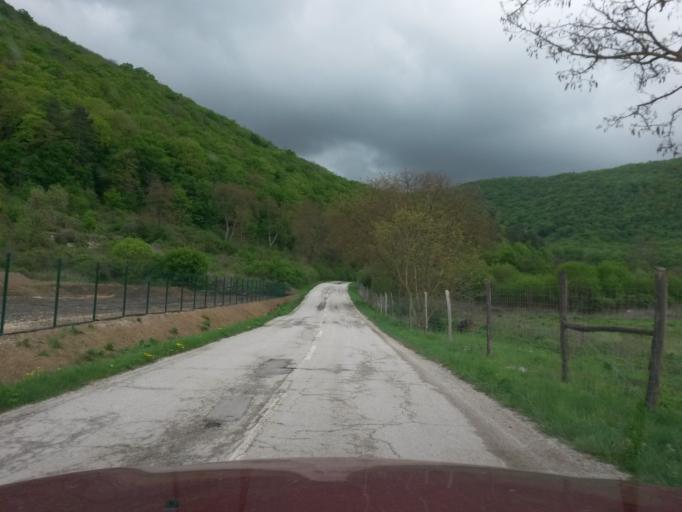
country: SK
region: Kosicky
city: Roznava
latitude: 48.5695
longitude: 20.4658
